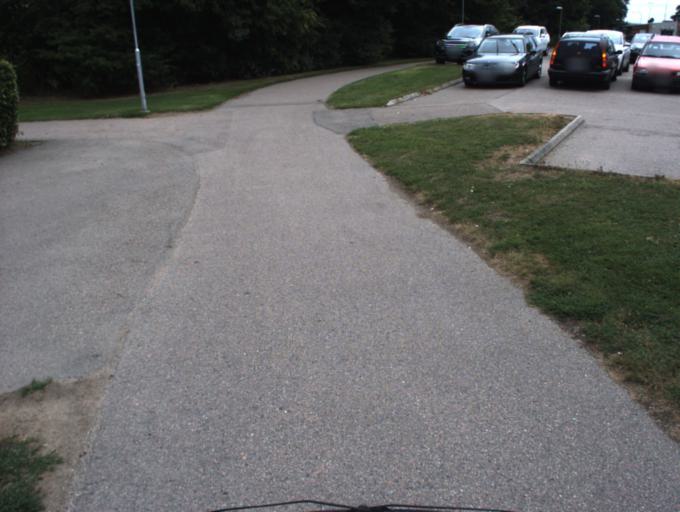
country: SE
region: Skane
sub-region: Helsingborg
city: Helsingborg
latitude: 56.0328
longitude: 12.7394
